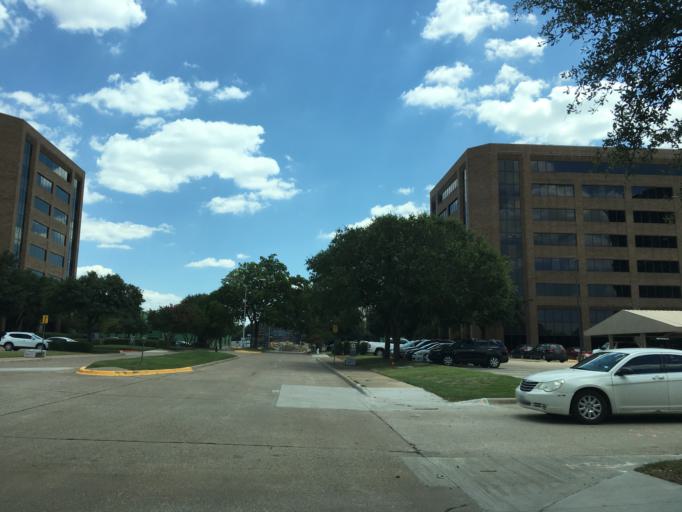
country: US
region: Texas
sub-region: Dallas County
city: Addison
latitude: 32.9315
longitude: -96.8418
